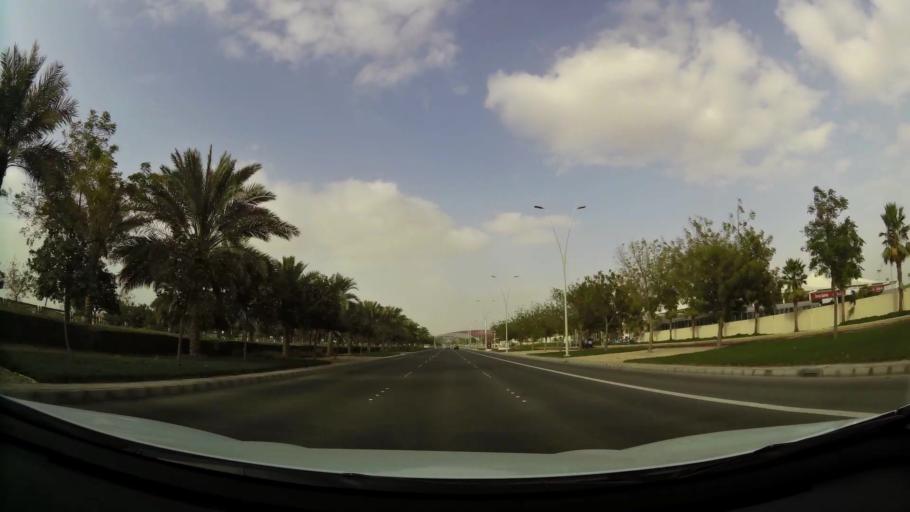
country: AE
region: Abu Dhabi
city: Abu Dhabi
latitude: 24.4736
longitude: 54.6019
